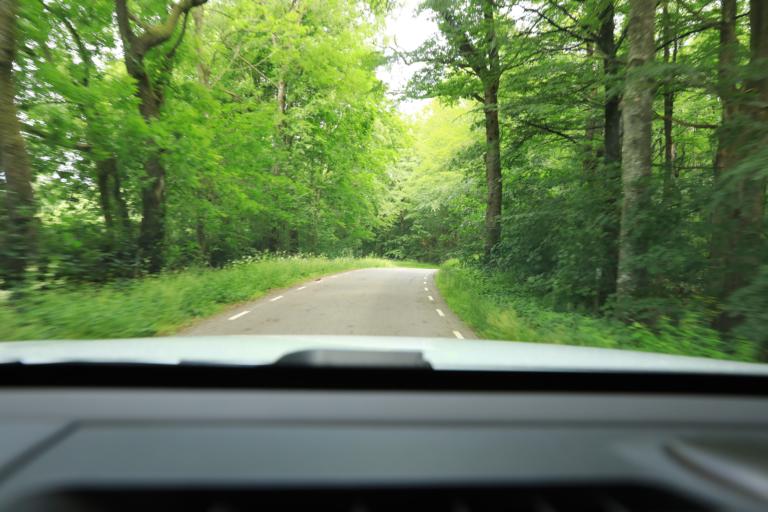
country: SE
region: Halland
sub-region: Varbergs Kommun
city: Tvaaker
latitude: 57.0431
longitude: 12.4673
